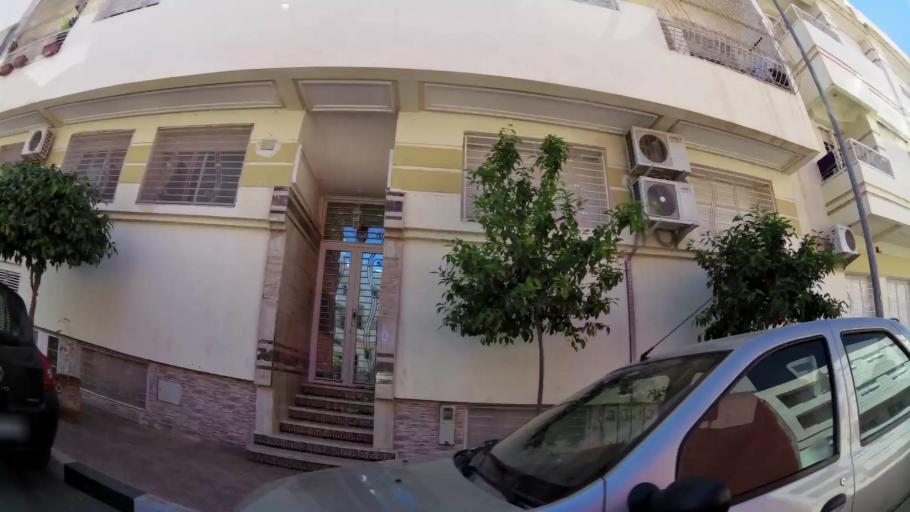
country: MA
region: Fes-Boulemane
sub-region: Fes
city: Fes
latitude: 34.0154
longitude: -5.0016
